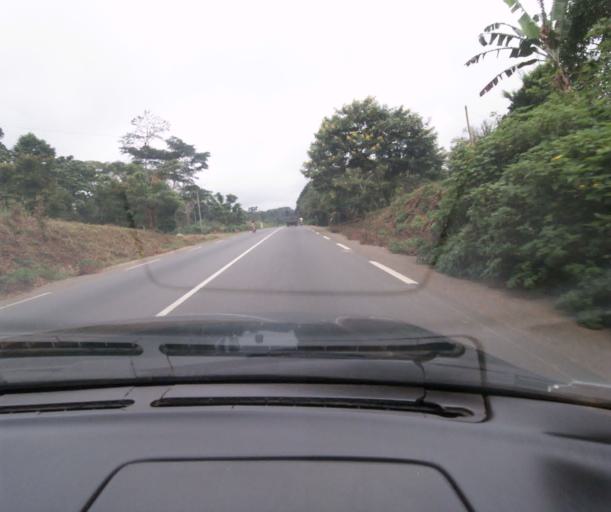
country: CM
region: Centre
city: Obala
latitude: 4.2103
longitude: 11.4447
